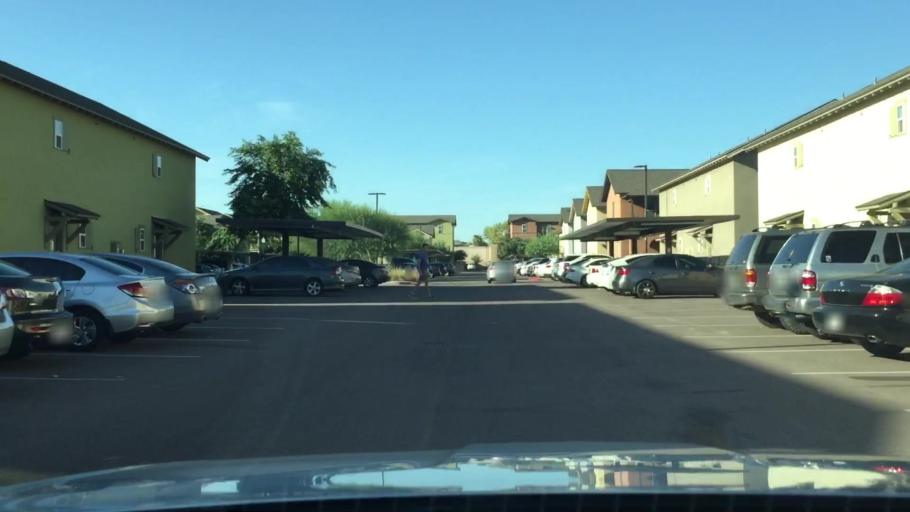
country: US
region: Arizona
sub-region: Maricopa County
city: Tempe Junction
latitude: 33.4235
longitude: -111.9657
